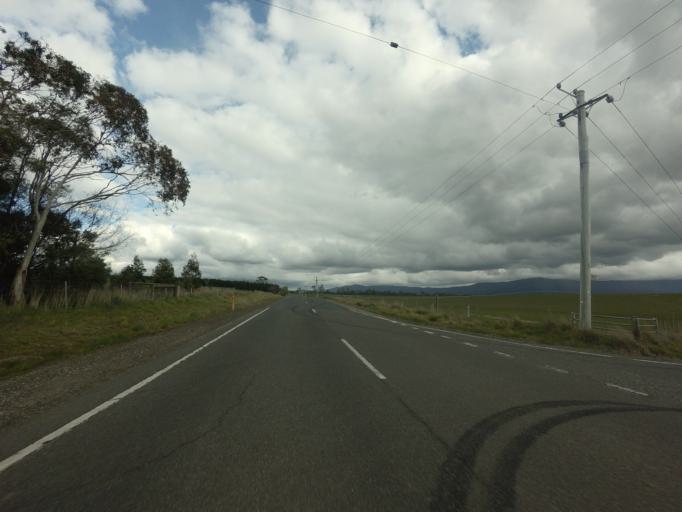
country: AU
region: Tasmania
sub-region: Northern Midlands
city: Longford
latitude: -41.7556
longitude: 147.0825
